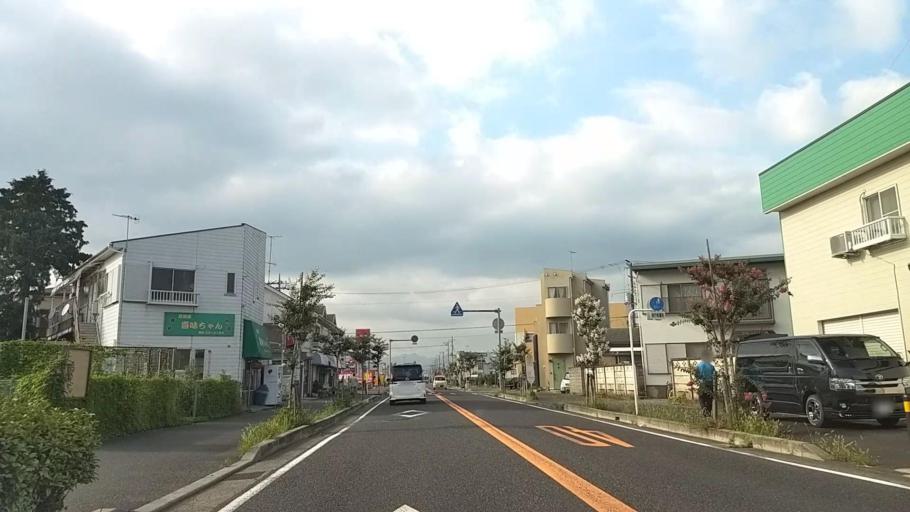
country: JP
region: Kanagawa
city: Isehara
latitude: 35.3601
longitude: 139.3256
